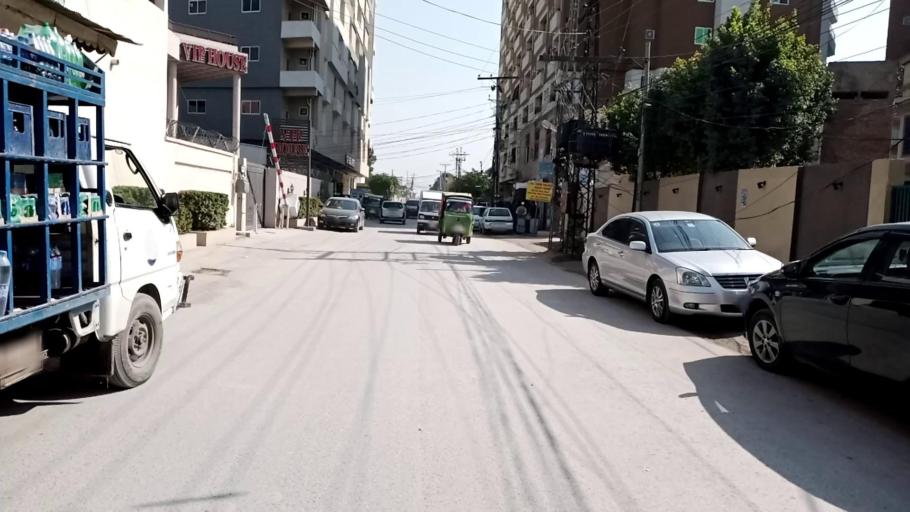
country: PK
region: Khyber Pakhtunkhwa
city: Peshawar
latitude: 33.9950
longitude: 71.5055
